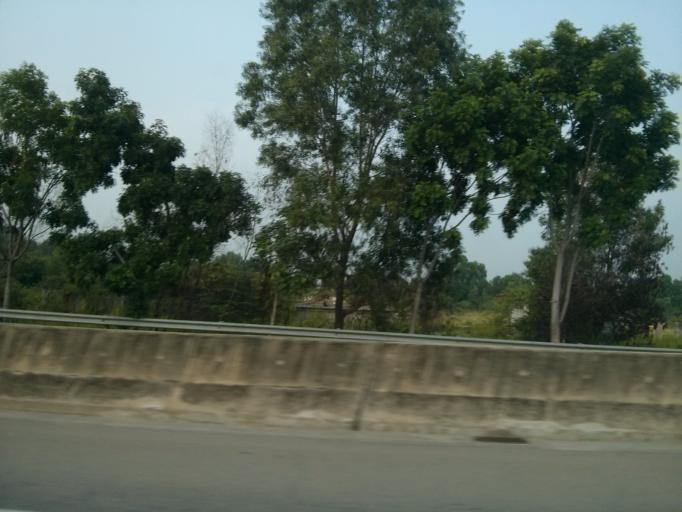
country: MY
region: Putrajaya
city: Putrajaya
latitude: 2.8788
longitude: 101.6648
